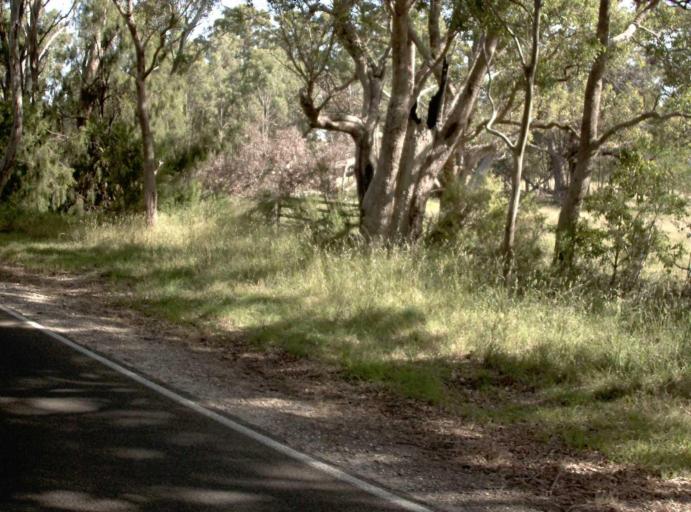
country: AU
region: Victoria
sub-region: East Gippsland
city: Lakes Entrance
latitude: -37.8079
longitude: 147.8425
